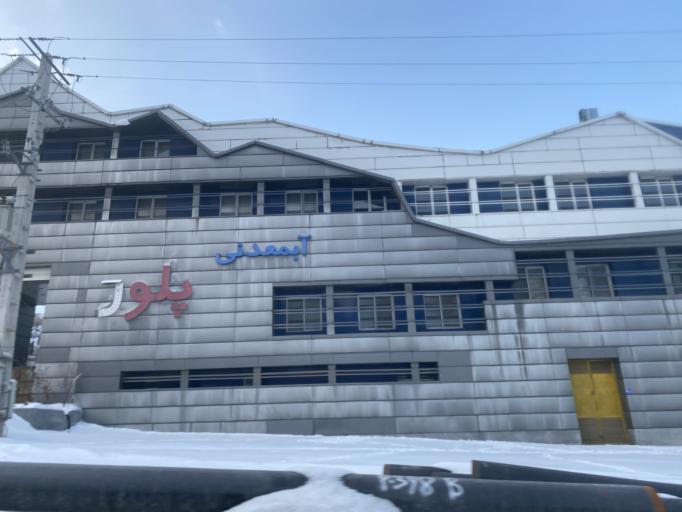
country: IR
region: Tehran
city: Damavand
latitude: 35.8327
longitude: 52.0335
